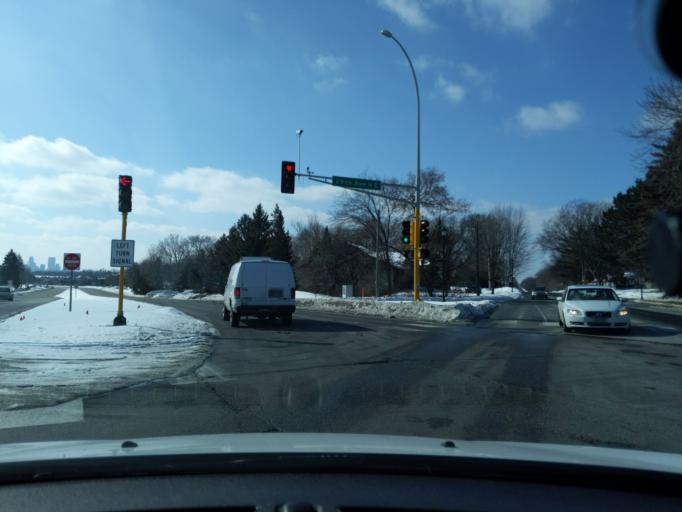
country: US
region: Minnesota
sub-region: Hennepin County
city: Saint Anthony
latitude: 45.0206
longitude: -93.2125
